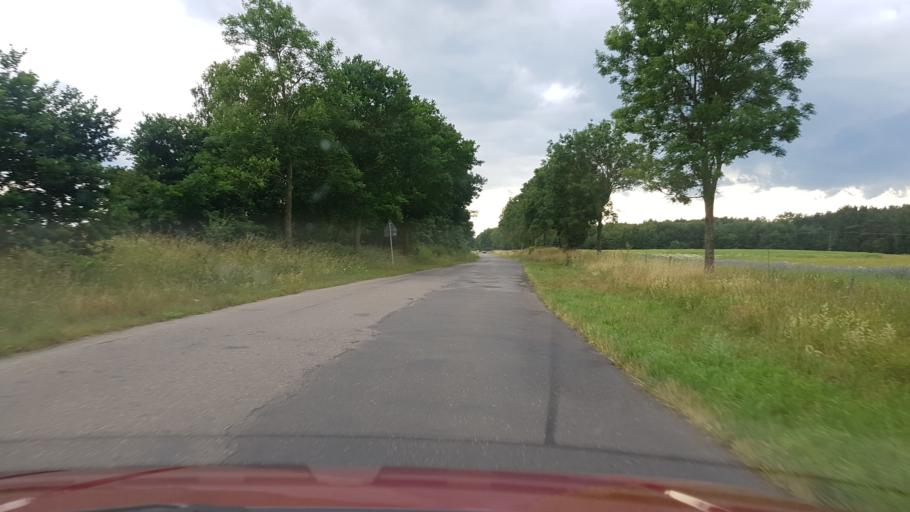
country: PL
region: West Pomeranian Voivodeship
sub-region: Powiat gryficki
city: Gryfice
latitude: 53.8749
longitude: 15.1311
